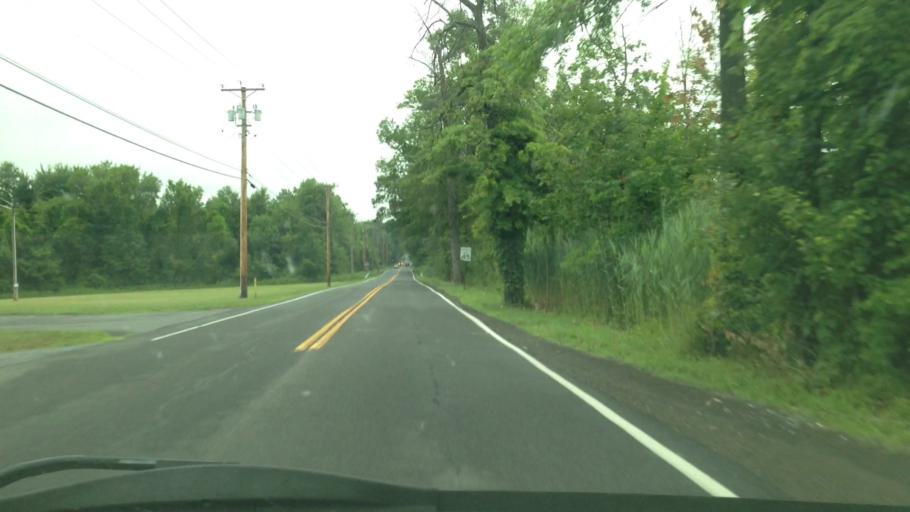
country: US
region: New York
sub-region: Ulster County
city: New Paltz
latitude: 41.7454
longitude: -74.0646
